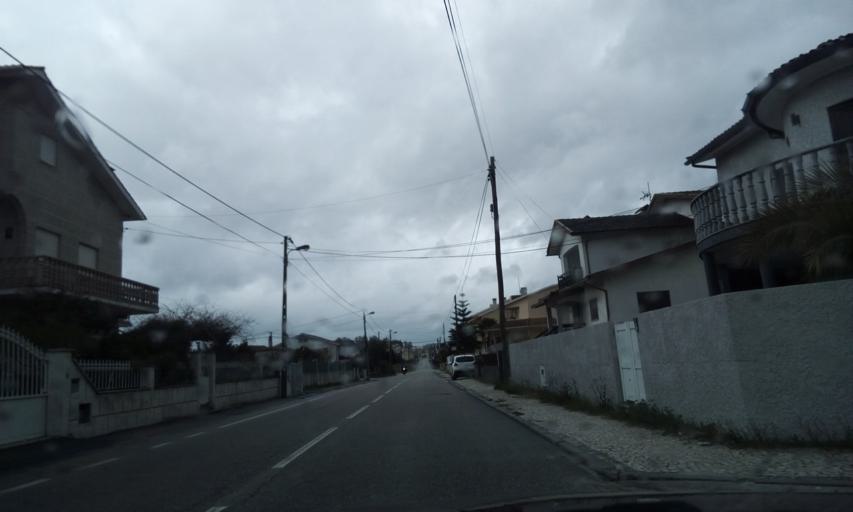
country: PT
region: Viseu
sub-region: Viseu
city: Rio de Loba
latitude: 40.6313
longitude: -7.8653
